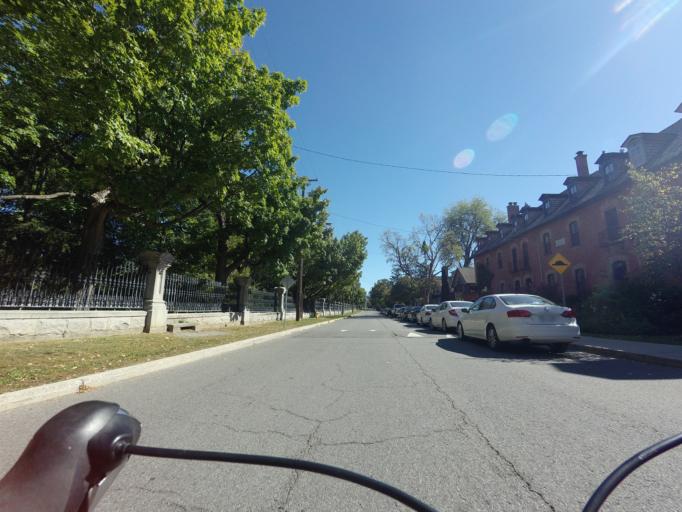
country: CA
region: Ontario
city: Ottawa
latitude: 45.4420
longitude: -75.6870
